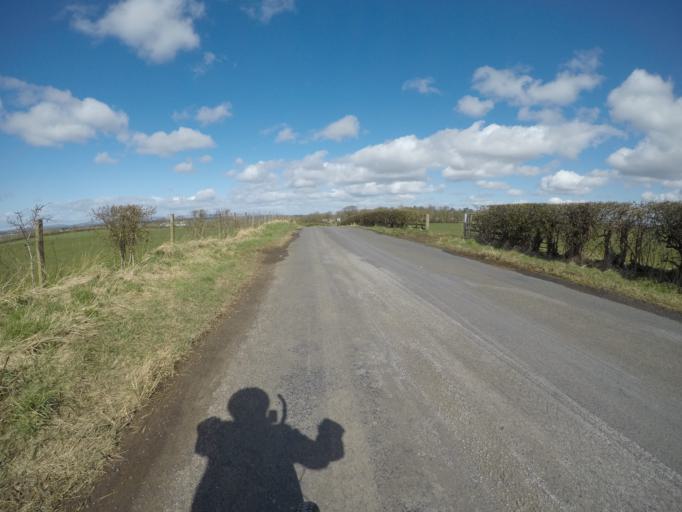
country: GB
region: Scotland
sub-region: East Ayrshire
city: Crosshouse
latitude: 55.6074
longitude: -4.5757
